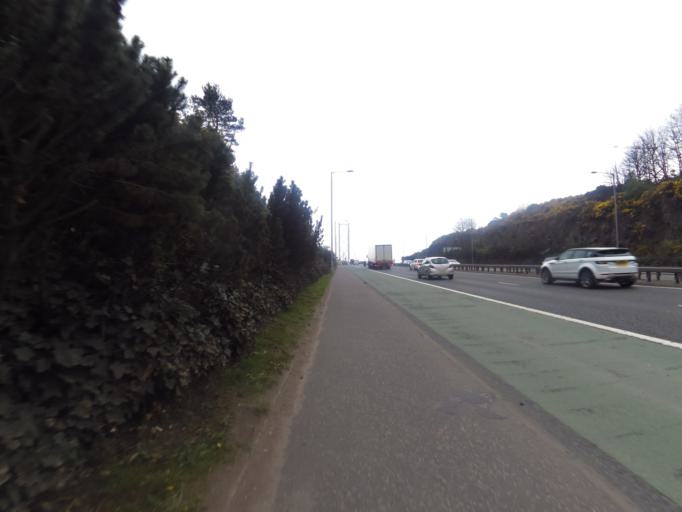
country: GB
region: Scotland
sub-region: Fife
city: North Queensferry
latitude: 56.0136
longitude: -3.4033
